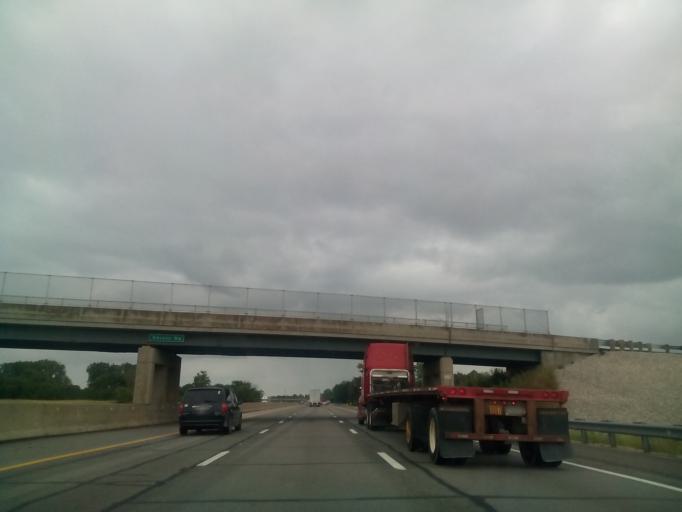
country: US
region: Ohio
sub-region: Sandusky County
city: Fremont
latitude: 41.3840
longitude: -83.0320
